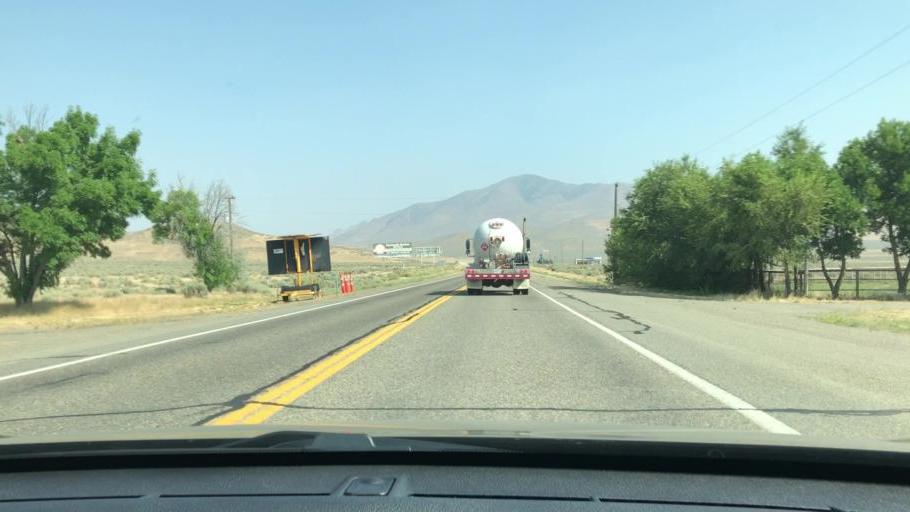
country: US
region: Nevada
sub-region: Humboldt County
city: Winnemucca
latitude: 41.2795
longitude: -117.6909
